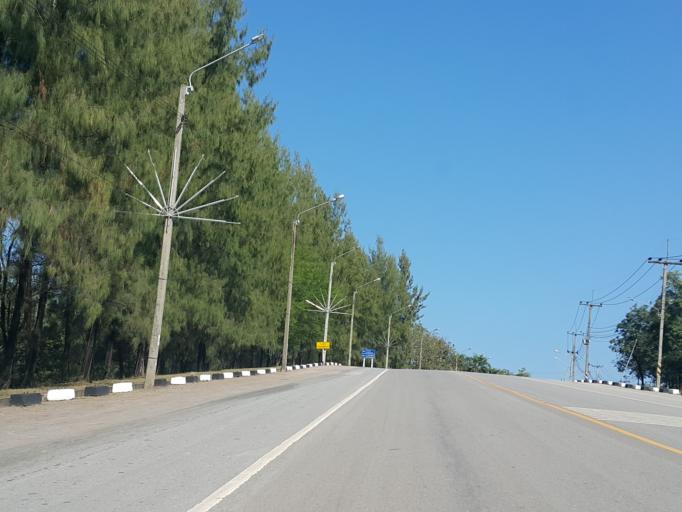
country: TH
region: Lampang
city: Mae Mo
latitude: 18.3146
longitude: 99.7445
